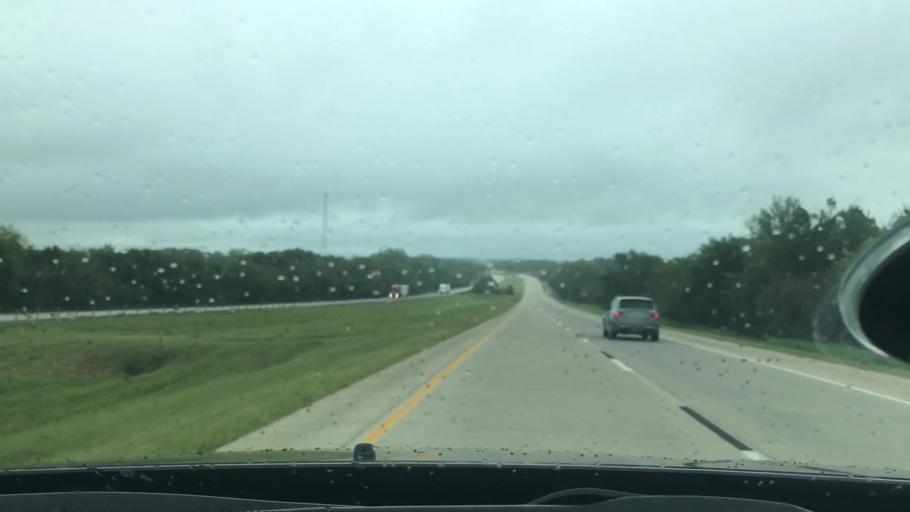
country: US
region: Oklahoma
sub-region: Okmulgee County
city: Henryetta
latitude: 35.4309
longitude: -95.9199
